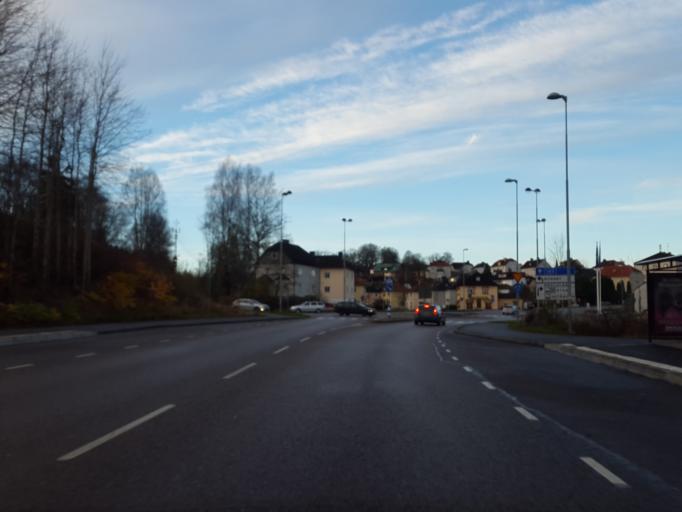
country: SE
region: Vaestra Goetaland
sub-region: Boras Kommun
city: Boras
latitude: 57.7261
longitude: 12.9240
